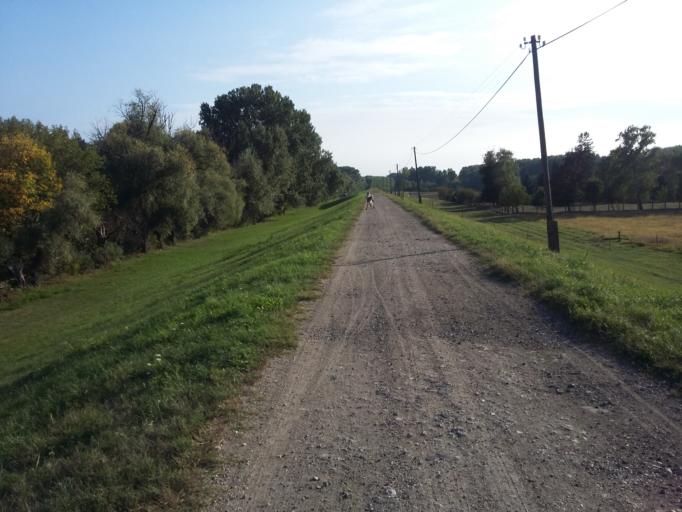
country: HU
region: Csongrad
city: Szeged
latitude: 46.2133
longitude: 20.1199
